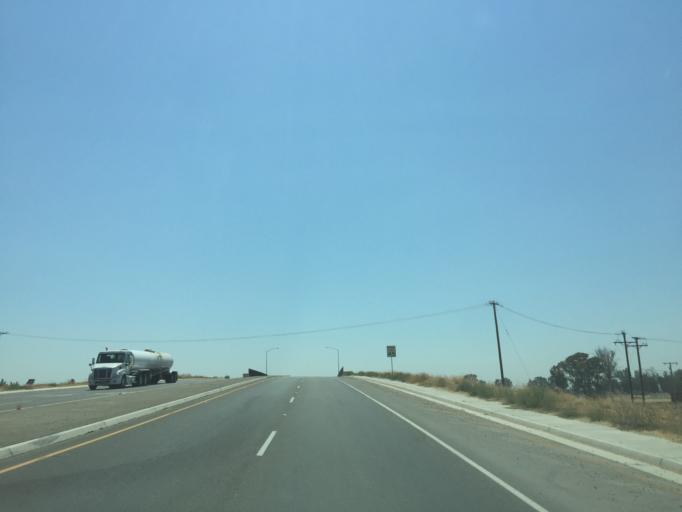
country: US
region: California
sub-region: Tulare County
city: Goshen
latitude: 36.3541
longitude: -119.4201
